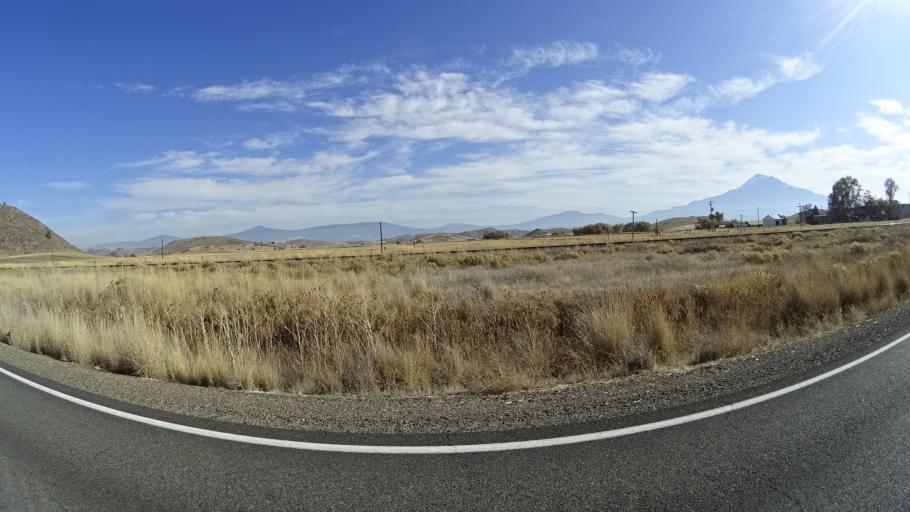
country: US
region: California
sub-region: Siskiyou County
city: Weed
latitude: 41.5284
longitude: -122.5229
